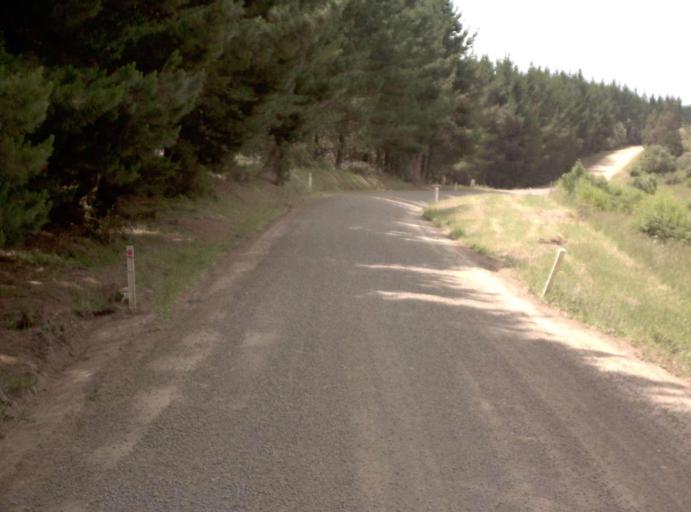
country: AU
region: Victoria
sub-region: Latrobe
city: Traralgon
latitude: -38.4147
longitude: 146.6176
